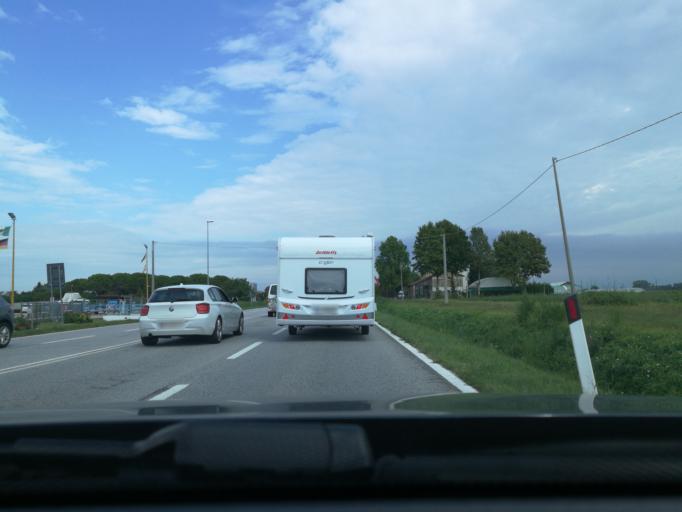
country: IT
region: Friuli Venezia Giulia
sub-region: Provincia di Udine
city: Pertegada
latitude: 45.7064
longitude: 13.0555
